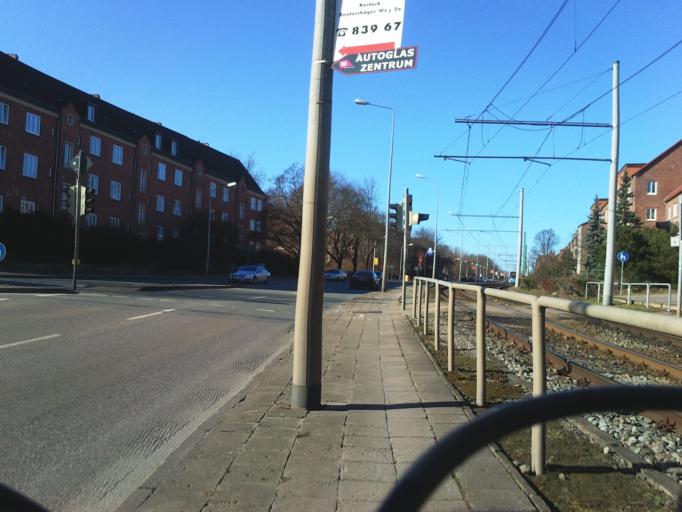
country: DE
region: Mecklenburg-Vorpommern
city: Rostock
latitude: 54.0933
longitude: 12.0959
